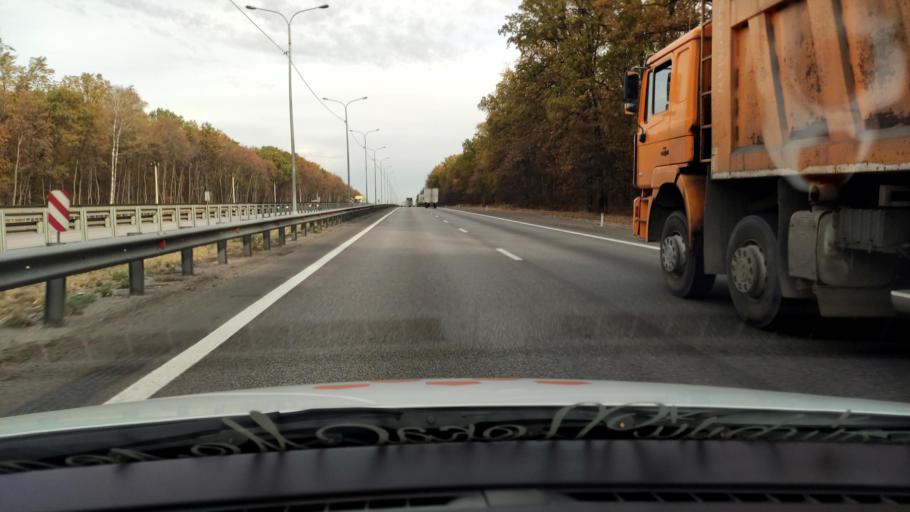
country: RU
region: Voronezj
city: Ramon'
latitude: 51.8764
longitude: 39.2169
